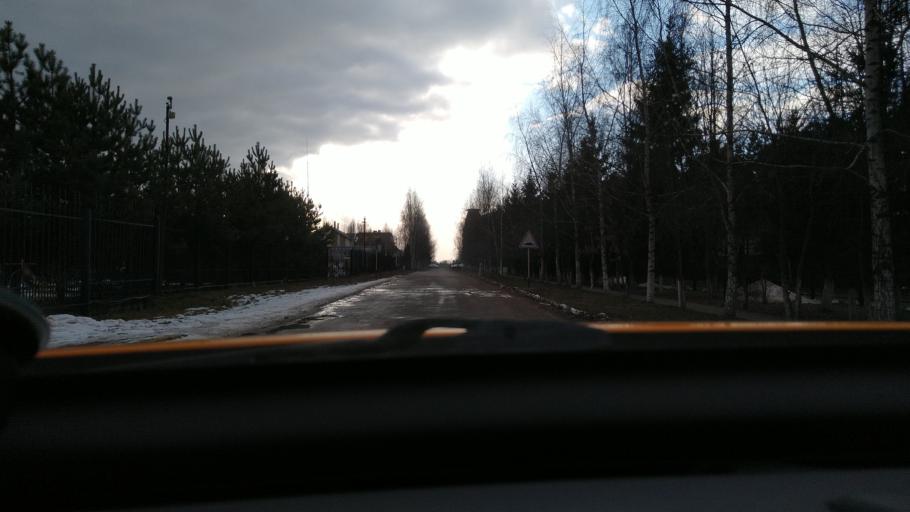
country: RU
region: Moskovskaya
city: Petrovo-Dal'neye
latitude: 55.7507
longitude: 37.1919
